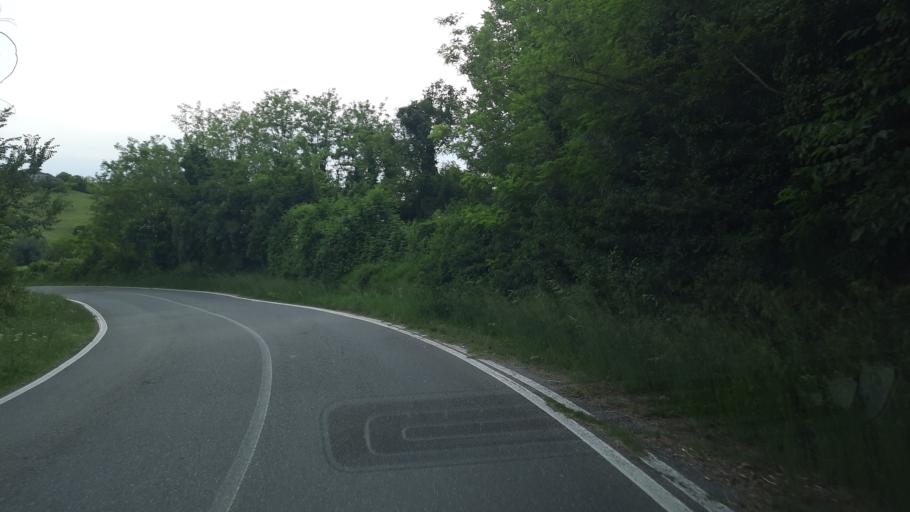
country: IT
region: Piedmont
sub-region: Provincia di Alessandria
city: Coniolo Bricco
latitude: 45.1433
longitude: 8.3809
